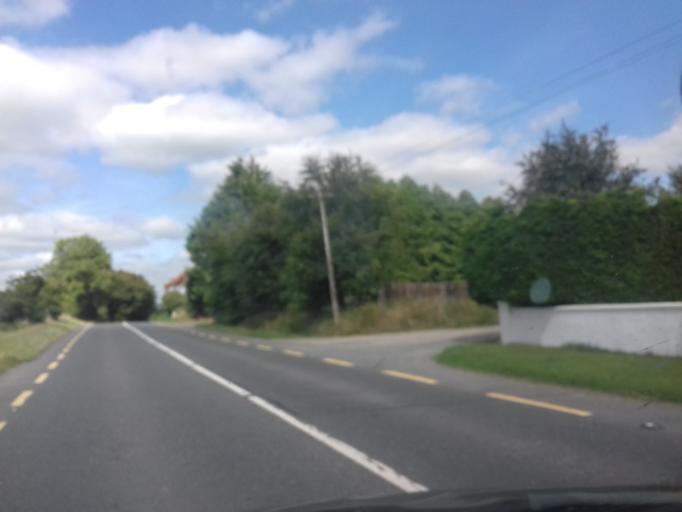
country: IE
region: Leinster
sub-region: Wicklow
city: Valleymount
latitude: 53.0479
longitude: -6.6329
